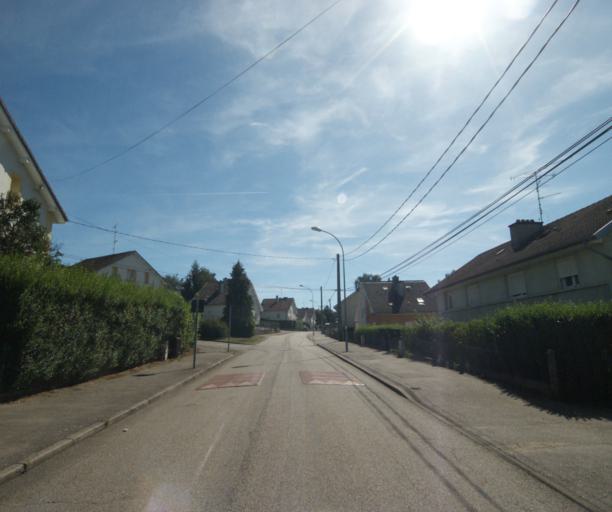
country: FR
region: Lorraine
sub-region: Departement des Vosges
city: Chantraine
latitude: 48.1849
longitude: 6.4340
